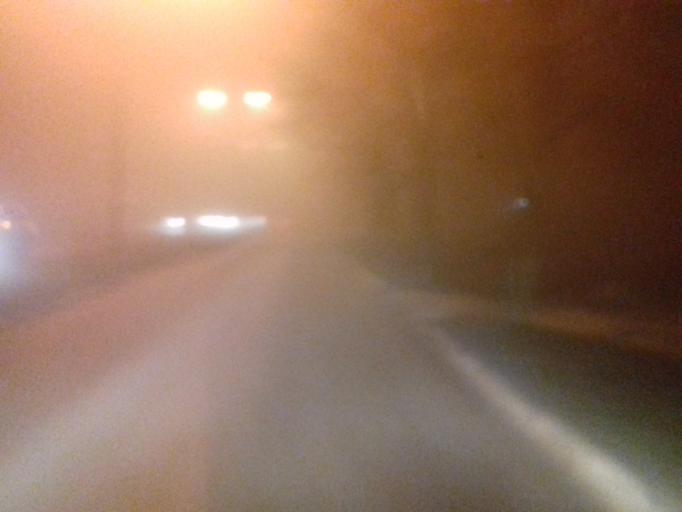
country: BA
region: Federation of Bosnia and Herzegovina
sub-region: Kanton Sarajevo
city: Sarajevo
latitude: 43.8303
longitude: 18.3559
